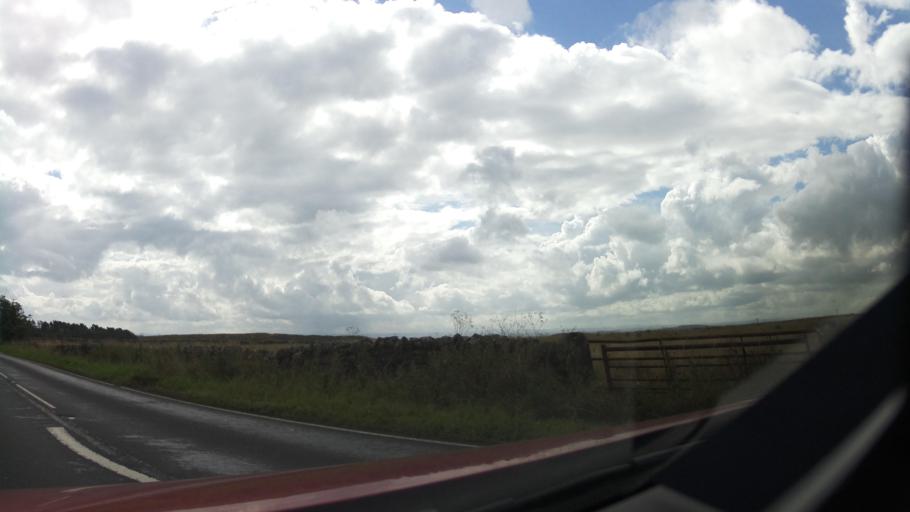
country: GB
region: England
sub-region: Northumberland
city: Birtley
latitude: 55.1026
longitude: -2.1233
